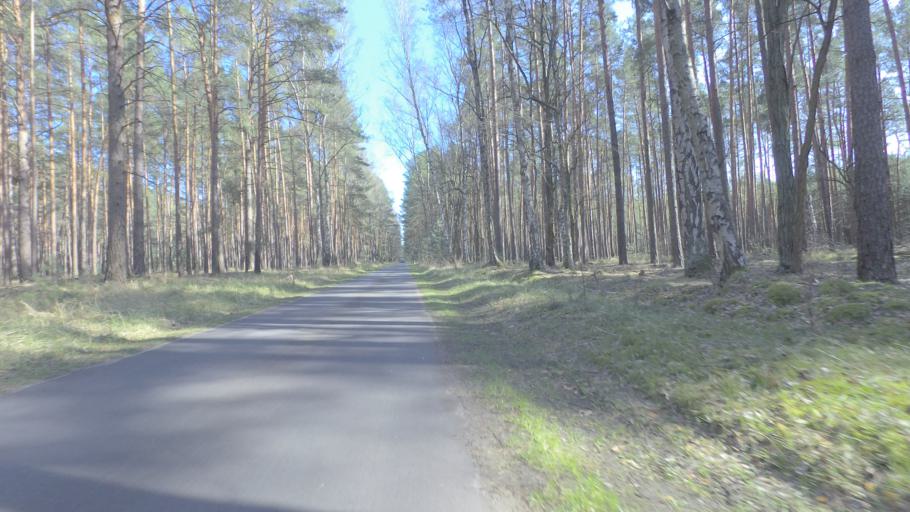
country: DE
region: Brandenburg
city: Halbe
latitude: 52.1712
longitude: 13.7521
